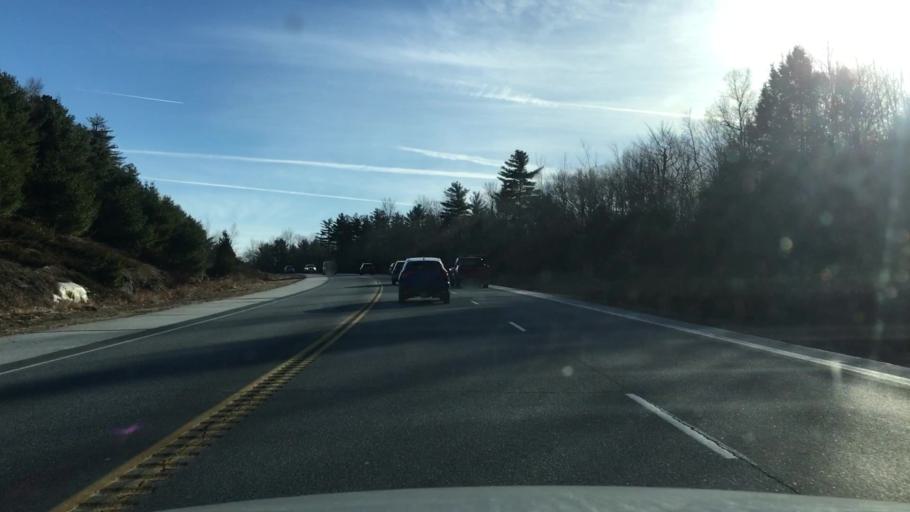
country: US
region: Maine
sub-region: Hancock County
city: Dedham
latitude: 44.6746
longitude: -68.5786
